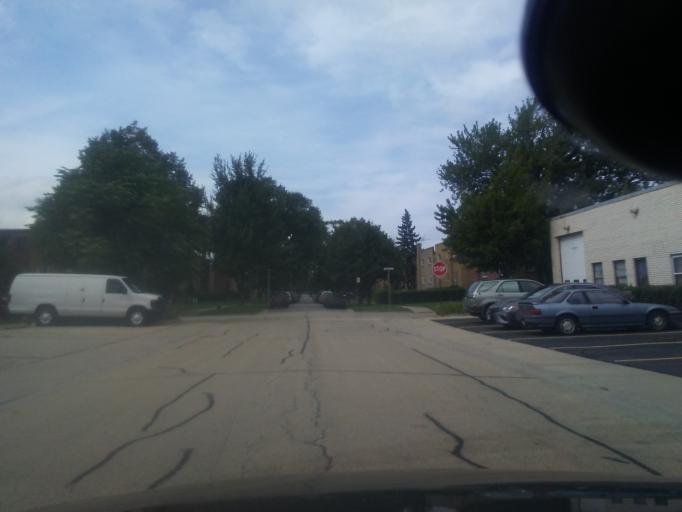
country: US
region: Illinois
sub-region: Cook County
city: Skokie
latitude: 42.0315
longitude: -87.7123
